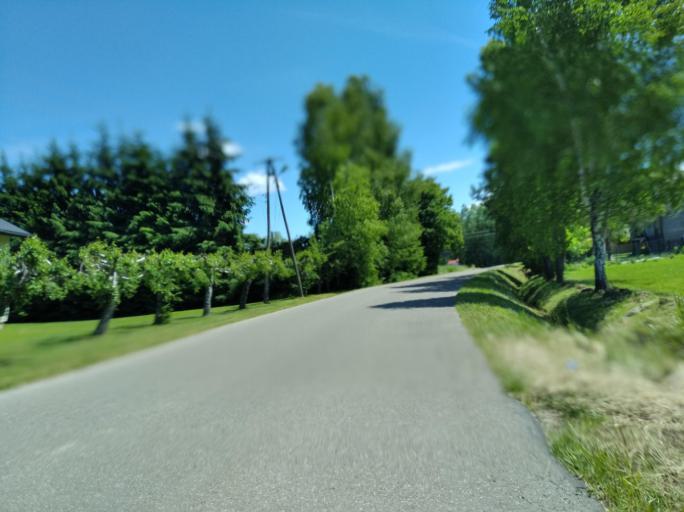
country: PL
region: Subcarpathian Voivodeship
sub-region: Powiat krosnienski
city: Wojaszowka
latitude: 49.7668
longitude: 21.6253
